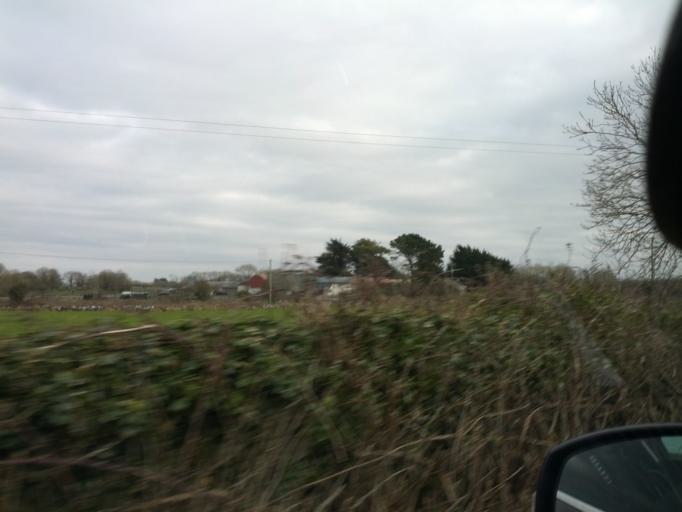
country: IE
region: Connaught
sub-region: County Galway
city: Oranmore
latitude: 53.2013
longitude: -8.9143
